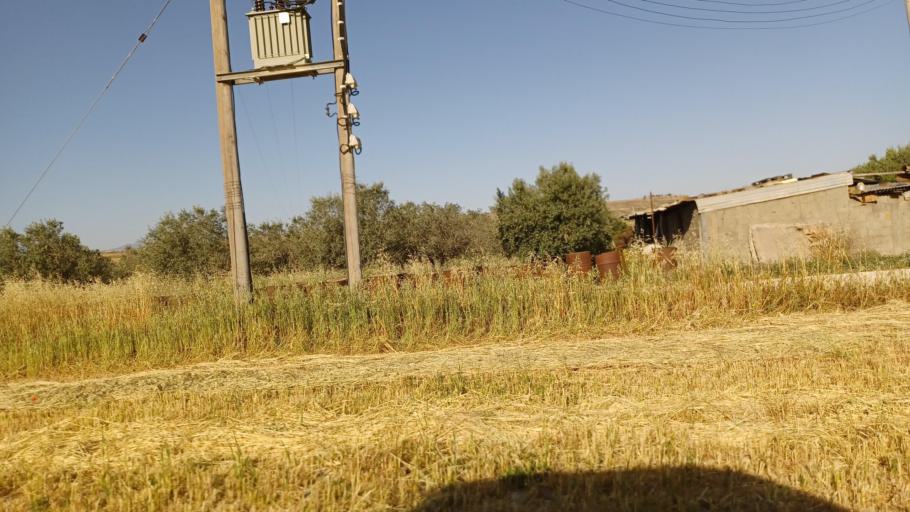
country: CY
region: Lefkosia
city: Mammari
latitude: 35.1654
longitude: 33.2495
